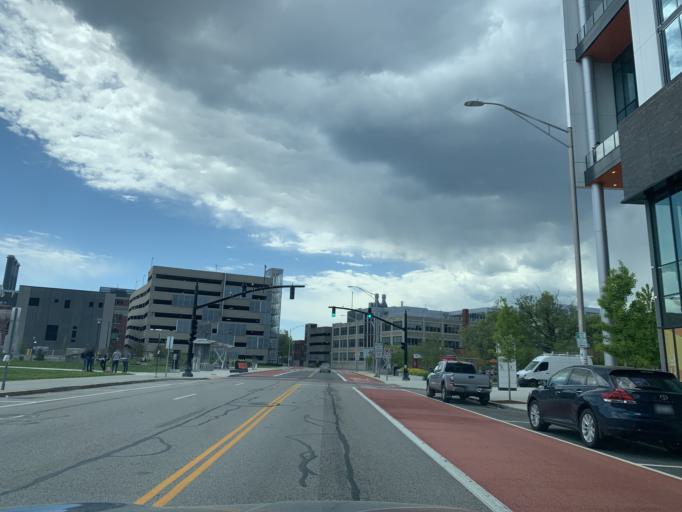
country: US
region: Rhode Island
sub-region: Providence County
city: Providence
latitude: 41.8204
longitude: -71.4081
